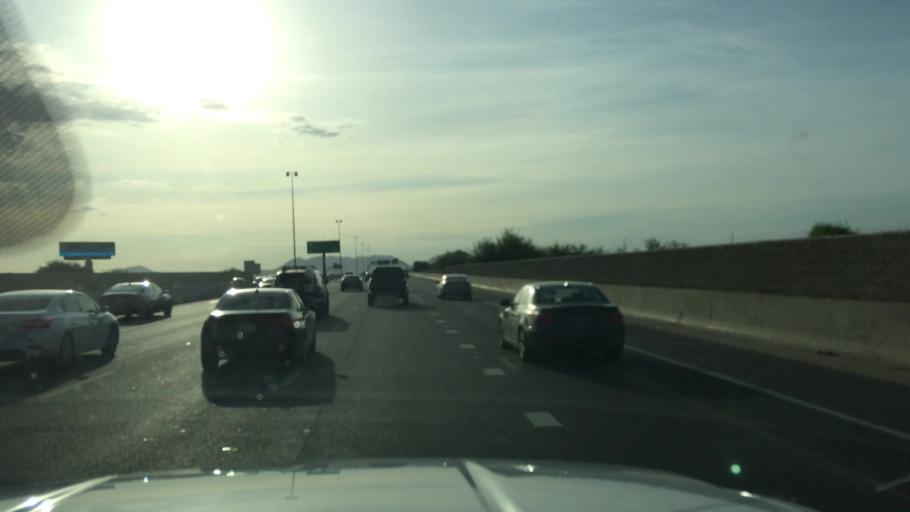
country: US
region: Arizona
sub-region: Maricopa County
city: Paradise Valley
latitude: 33.6742
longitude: -112.0161
